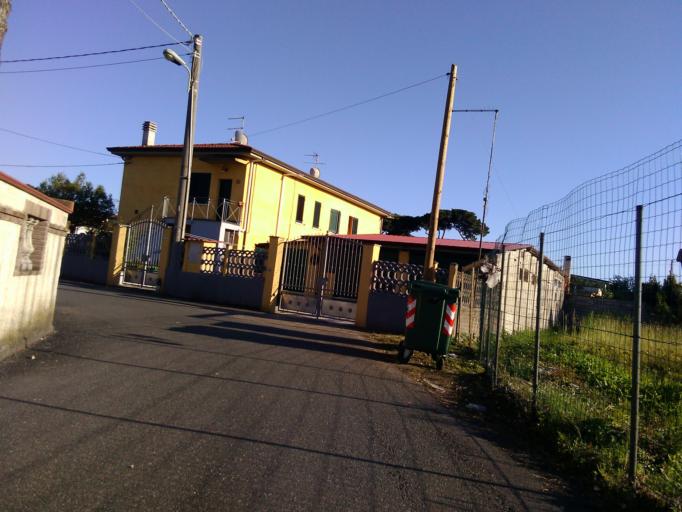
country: IT
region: Tuscany
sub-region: Provincia di Massa-Carrara
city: Massa
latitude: 44.0204
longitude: 10.0870
